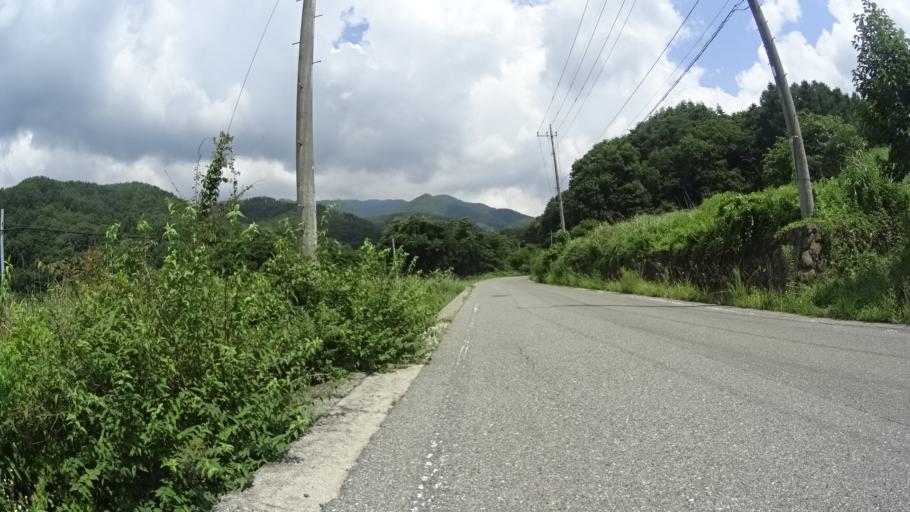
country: JP
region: Yamanashi
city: Nirasaki
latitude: 35.8805
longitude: 138.5201
